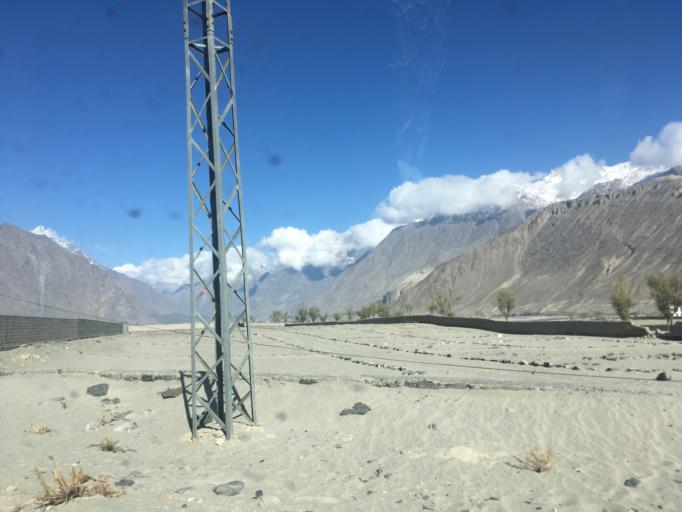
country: PK
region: Gilgit-Baltistan
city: Skardu
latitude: 35.3576
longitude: 75.5458
